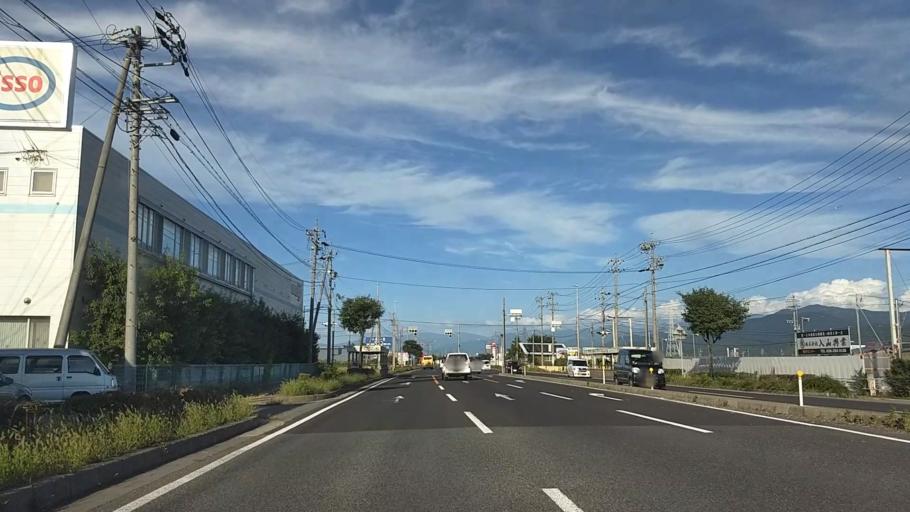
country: JP
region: Nagano
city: Nagano-shi
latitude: 36.5867
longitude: 138.1692
